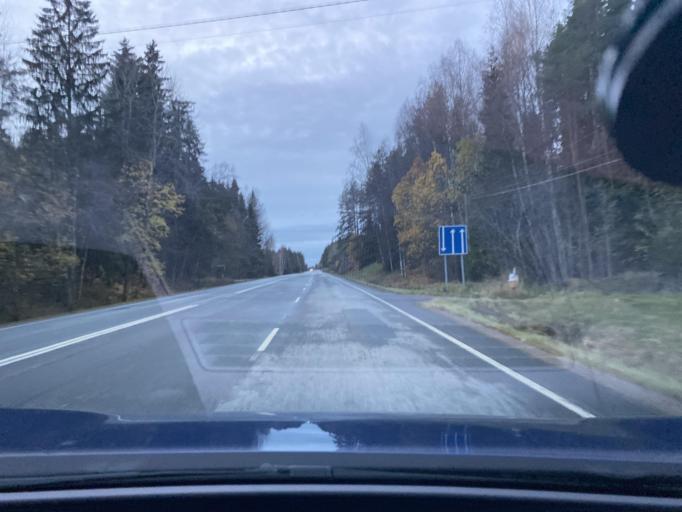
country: FI
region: Uusimaa
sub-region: Helsinki
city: Sammatti
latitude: 60.3852
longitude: 23.8714
